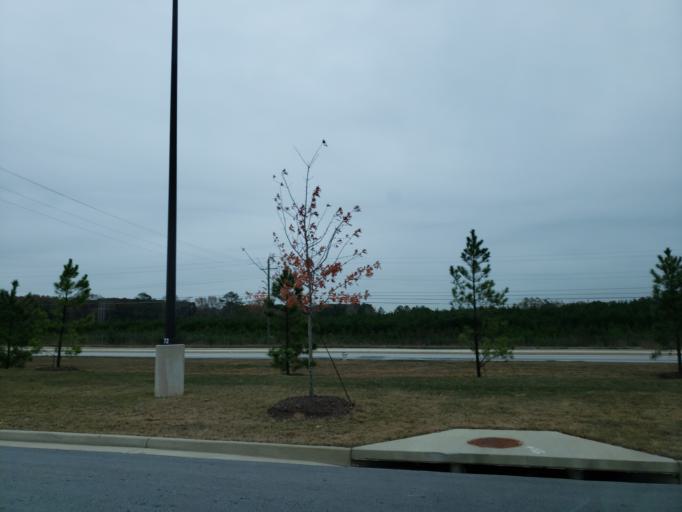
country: US
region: Georgia
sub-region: Cobb County
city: Mableton
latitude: 33.7850
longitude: -84.5061
